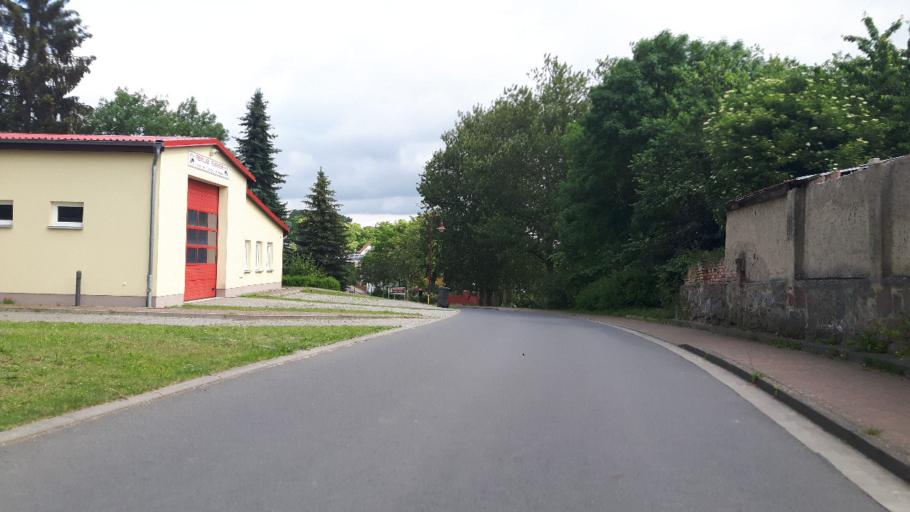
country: DE
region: Brandenburg
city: Mescherin
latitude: 53.2488
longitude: 14.4325
